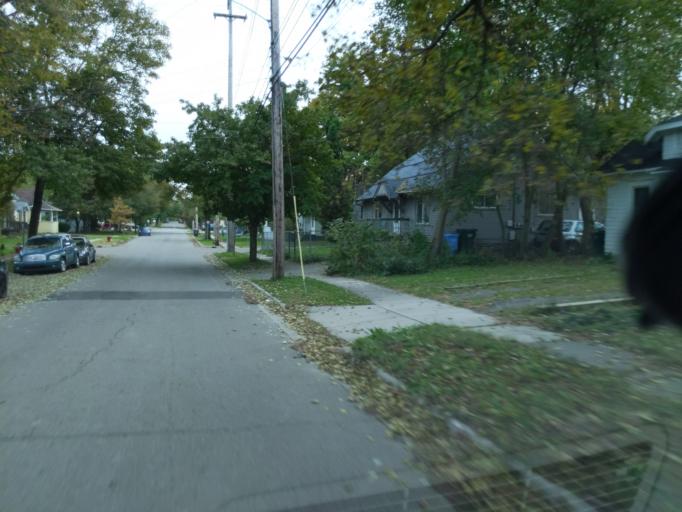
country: US
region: Michigan
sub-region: Ingham County
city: East Lansing
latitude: 42.7315
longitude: -84.5164
